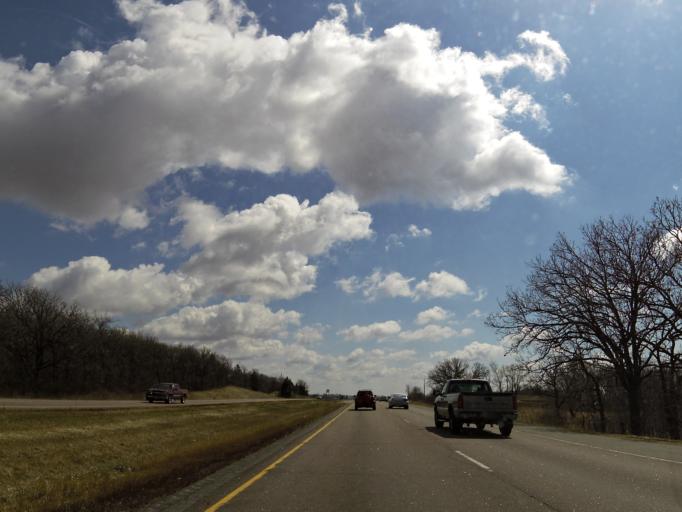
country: US
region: Minnesota
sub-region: Dakota County
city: Rosemount
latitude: 44.6902
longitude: -93.0217
